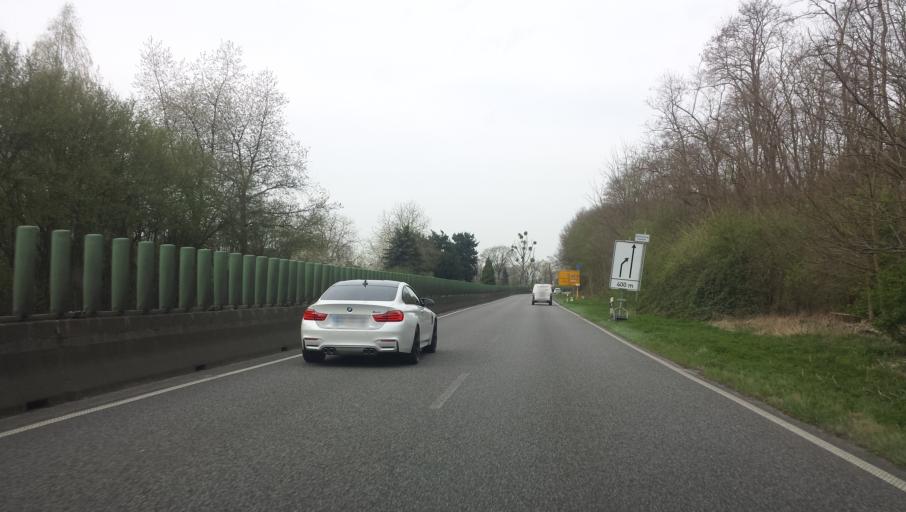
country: DE
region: Hesse
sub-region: Regierungsbezirk Darmstadt
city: Maintal
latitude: 50.1361
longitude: 8.8110
